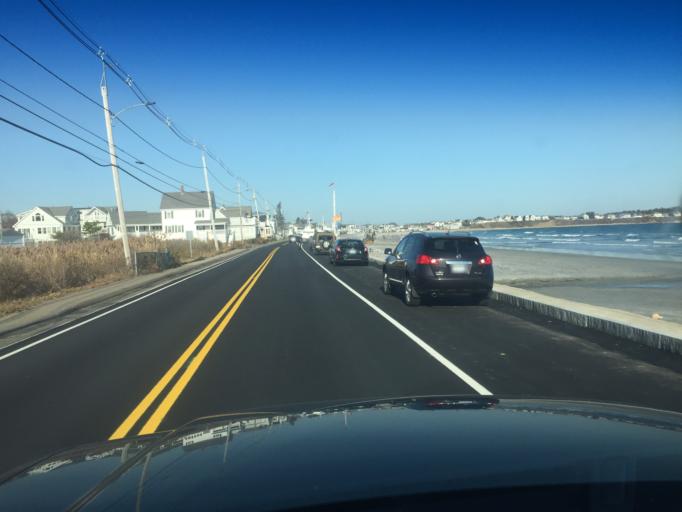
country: US
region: Maine
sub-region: York County
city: York Beach
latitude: 43.1613
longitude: -70.6205
